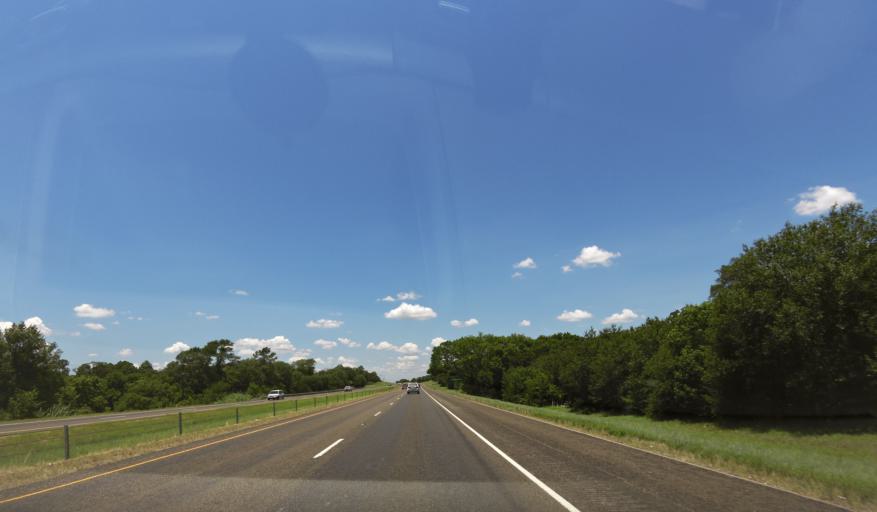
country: US
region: Texas
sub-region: Washington County
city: Brenham
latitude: 30.1823
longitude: -96.4810
